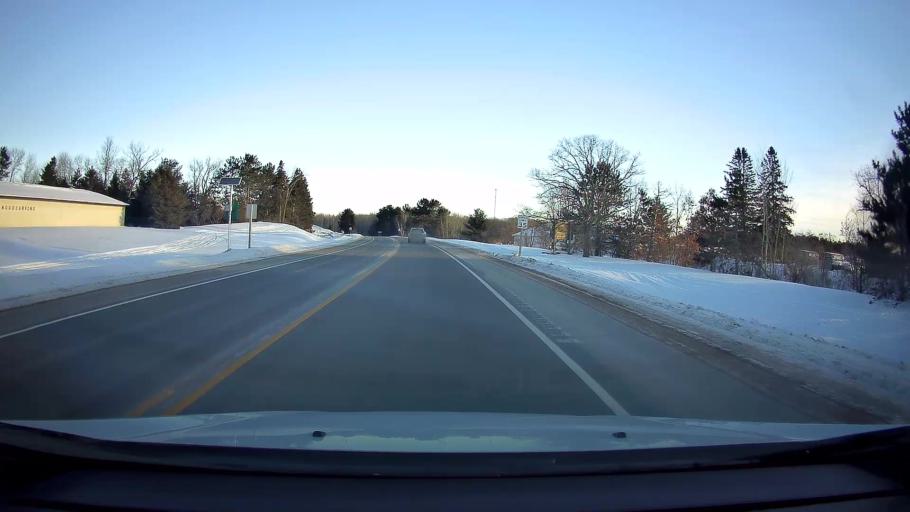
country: US
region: Wisconsin
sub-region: Washburn County
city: Shell Lake
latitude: 45.7482
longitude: -91.9183
